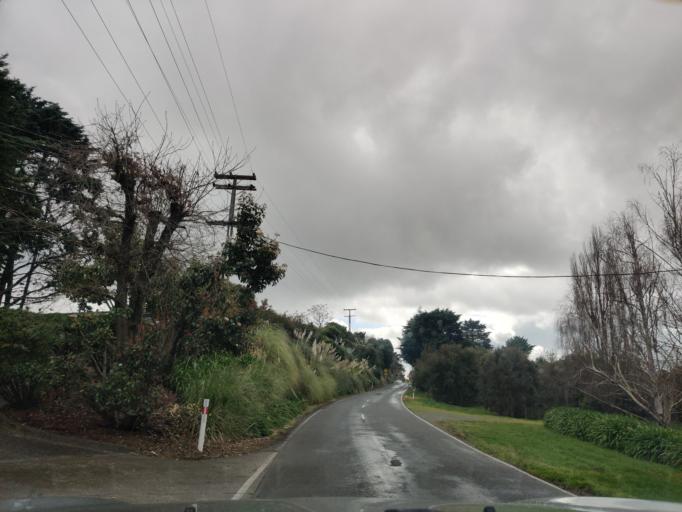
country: NZ
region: Hawke's Bay
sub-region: Hastings District
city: Hastings
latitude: -39.6866
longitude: 176.8982
